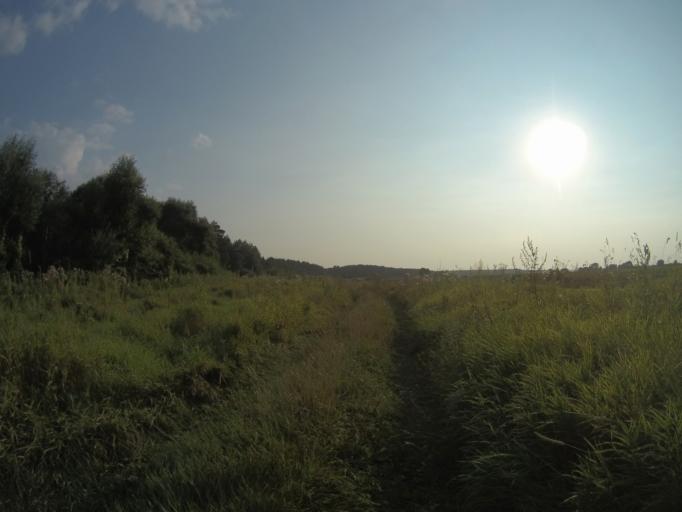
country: RU
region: Vladimir
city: Orgtrud
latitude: 56.3015
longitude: 40.6887
